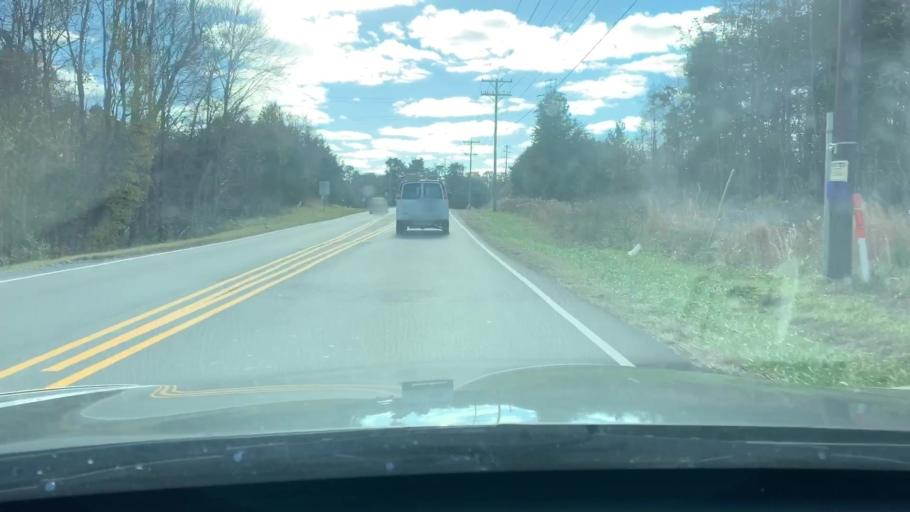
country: US
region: North Carolina
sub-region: Alamance County
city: Haw River
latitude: 36.0801
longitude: -79.3482
